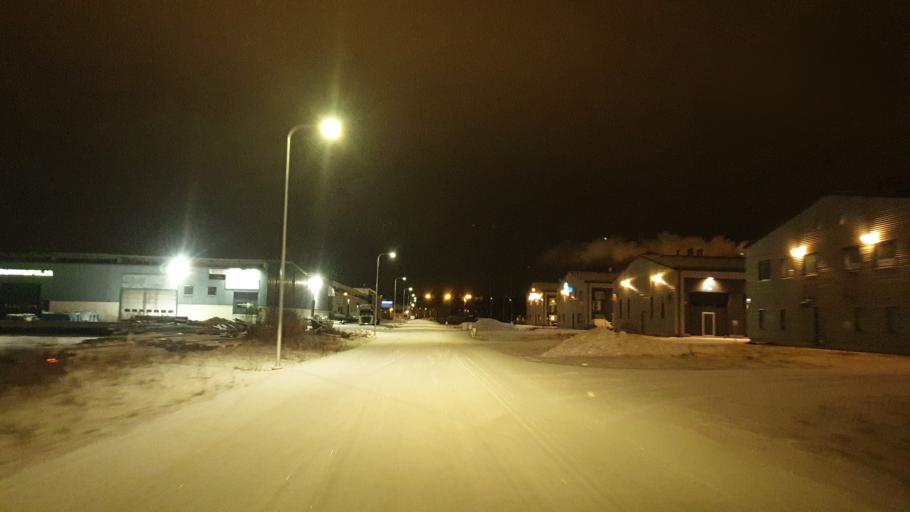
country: FI
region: Northern Ostrobothnia
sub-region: Oulu
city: Oulu
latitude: 64.9942
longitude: 25.4463
